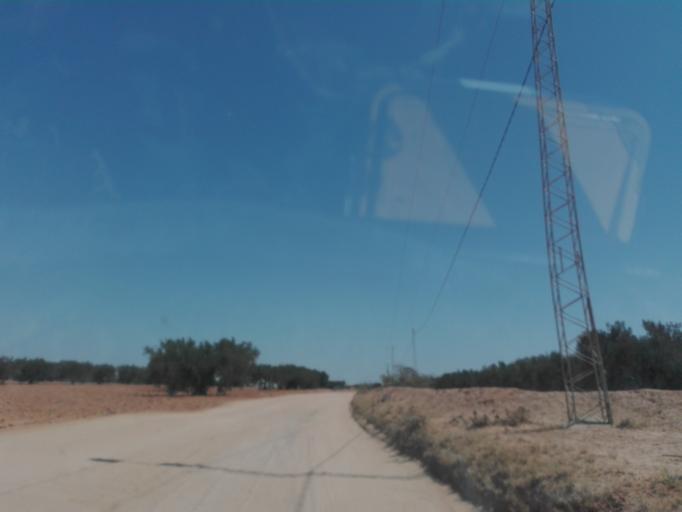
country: TN
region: Safaqis
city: Bi'r `Ali Bin Khalifah
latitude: 34.6691
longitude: 10.2362
